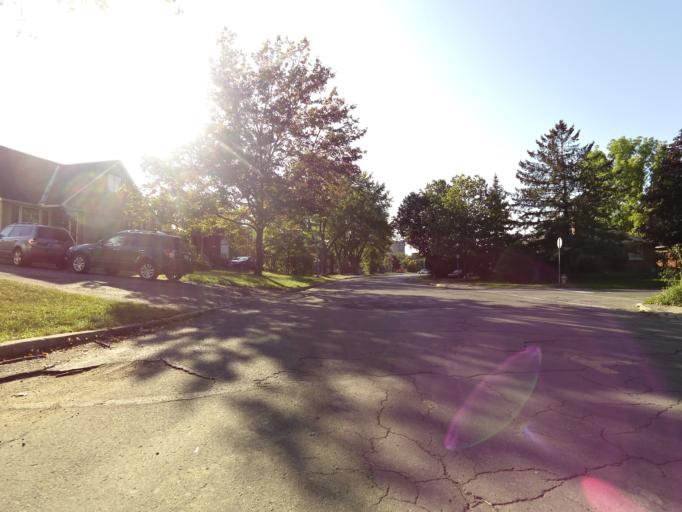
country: CA
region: Ontario
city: Ottawa
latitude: 45.4077
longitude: -75.6567
